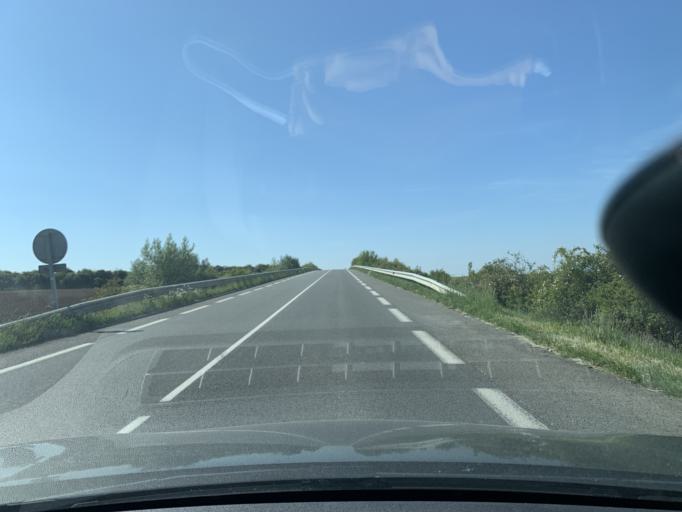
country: FR
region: Nord-Pas-de-Calais
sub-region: Departement du Nord
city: Cambrai
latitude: 50.1518
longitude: 3.2421
